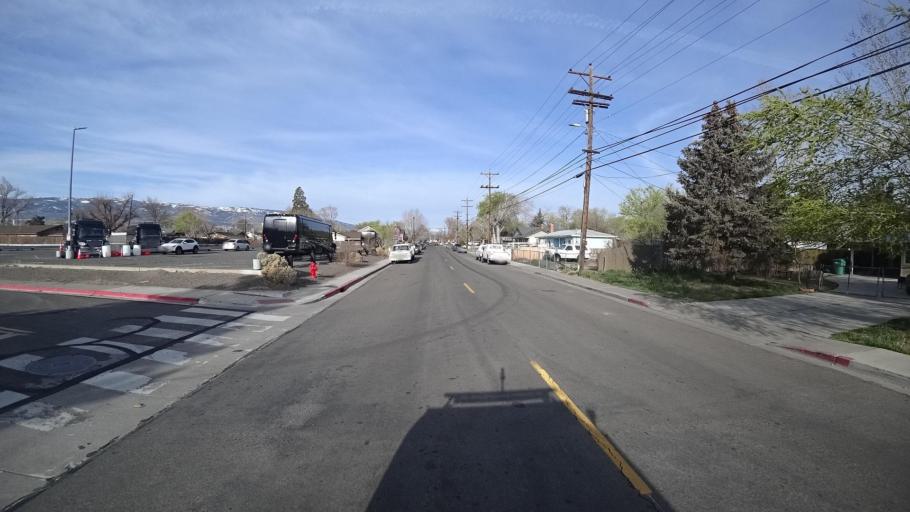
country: US
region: Nevada
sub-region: Washoe County
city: Reno
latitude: 39.5075
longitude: -119.7936
